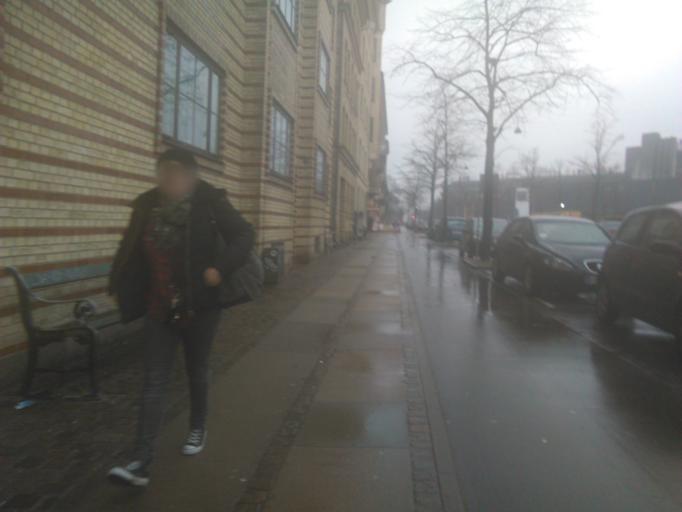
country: DK
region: Capital Region
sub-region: Kobenhavn
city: Copenhagen
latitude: 55.6928
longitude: 12.5609
